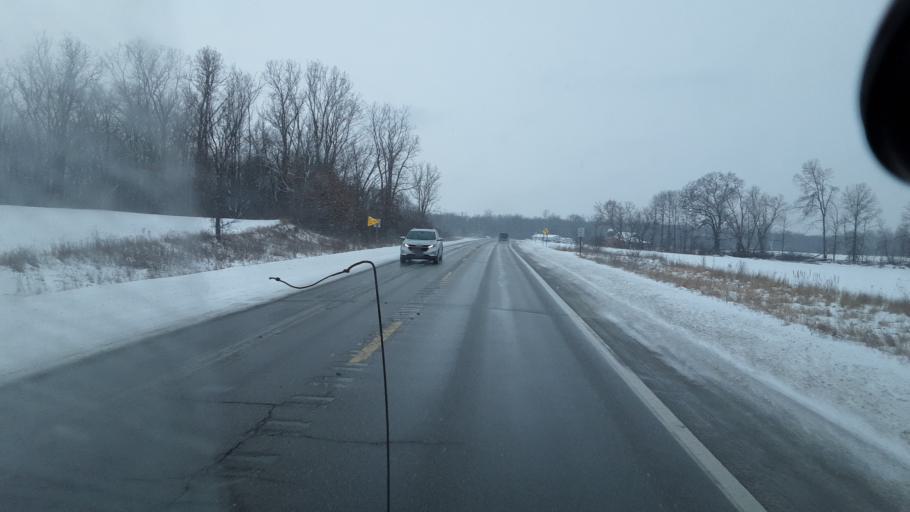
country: US
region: Michigan
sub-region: Jackson County
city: Jackson
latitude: 42.3163
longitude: -84.3821
